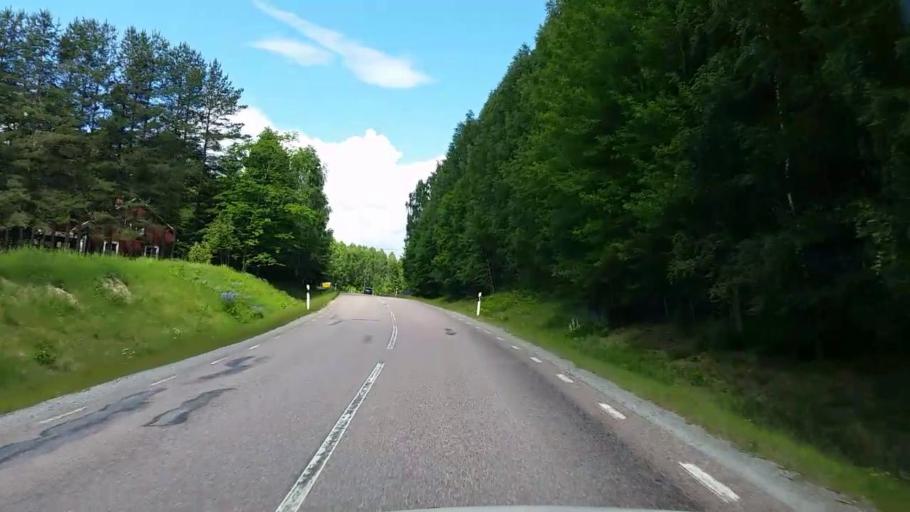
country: SE
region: Vaestmanland
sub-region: Fagersta Kommun
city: Fagersta
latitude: 59.9516
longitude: 15.7902
